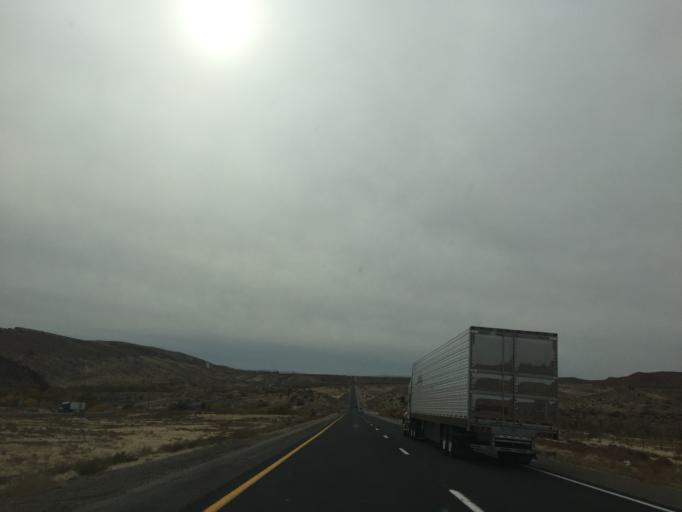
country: US
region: Utah
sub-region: Washington County
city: Hurricane
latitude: 37.2106
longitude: -113.3935
